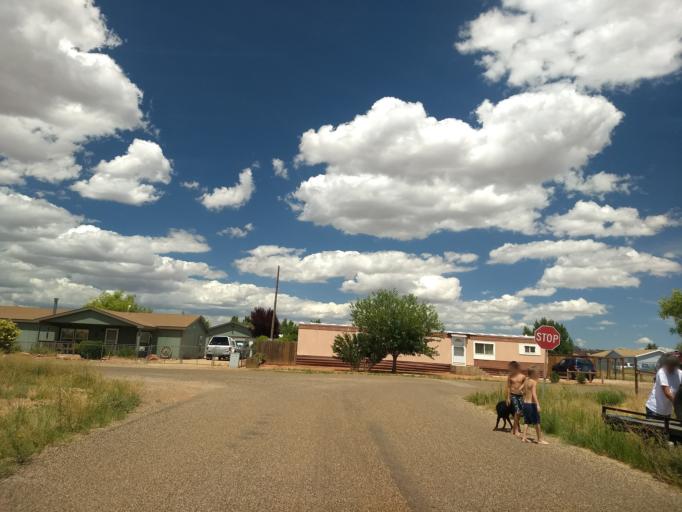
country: US
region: Arizona
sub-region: Coconino County
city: Fredonia
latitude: 36.9592
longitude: -112.5242
